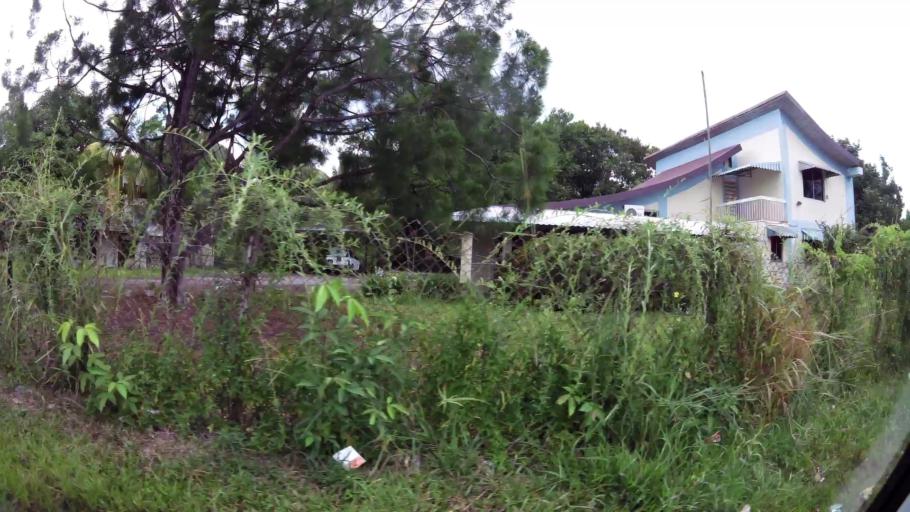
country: BN
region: Brunei and Muara
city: Bandar Seri Begawan
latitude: 4.9510
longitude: 114.9587
